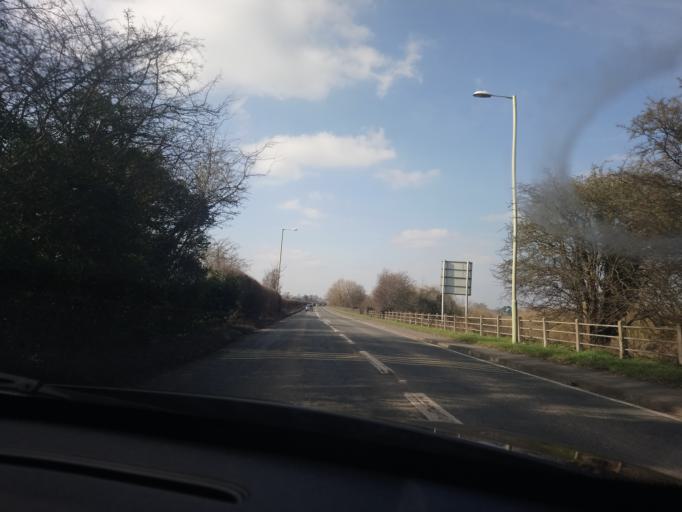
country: GB
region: England
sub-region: Shropshire
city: Berrington
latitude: 52.6801
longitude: -2.6844
